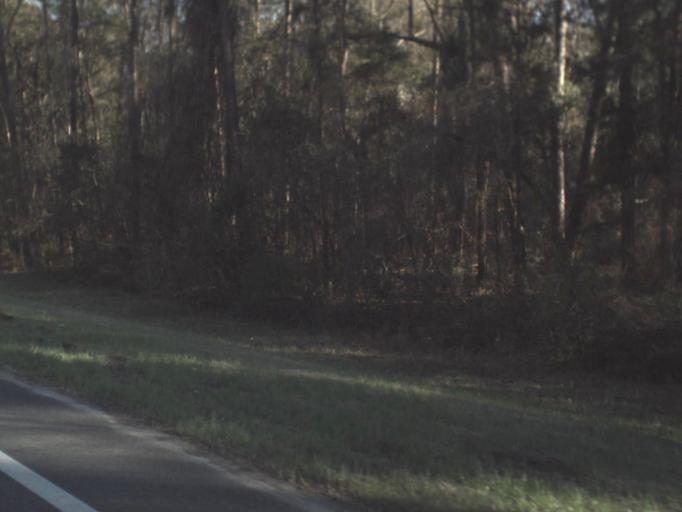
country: US
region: Florida
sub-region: Jackson County
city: Marianna
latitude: 30.7394
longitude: -85.1198
